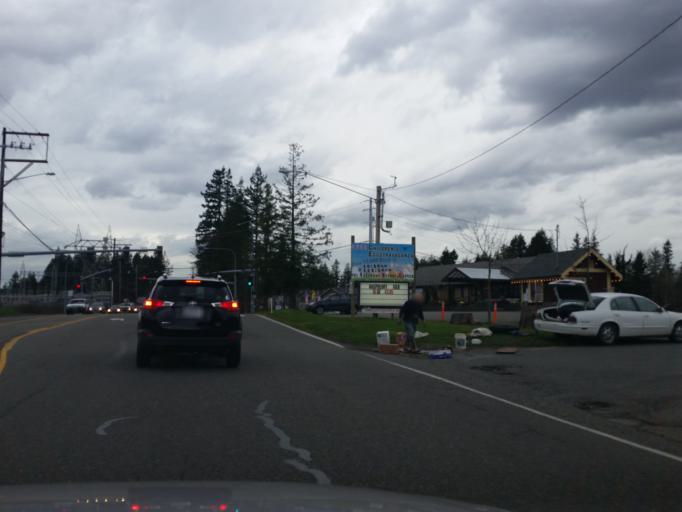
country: US
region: Washington
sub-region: Snohomish County
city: North Creek
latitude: 47.8128
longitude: -122.1808
